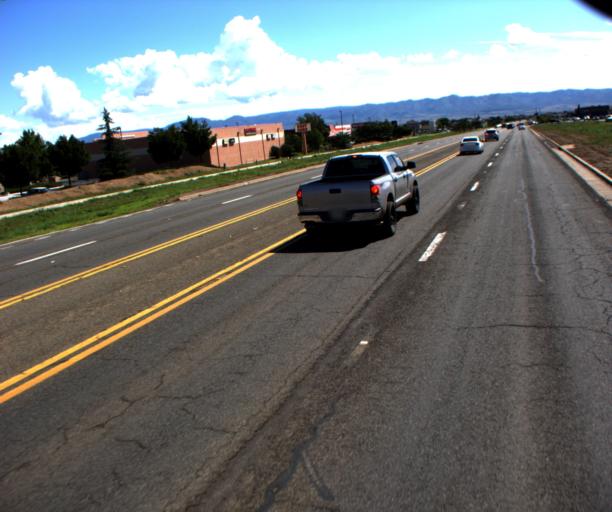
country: US
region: Arizona
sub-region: Yavapai County
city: Prescott Valley
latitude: 34.5839
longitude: -112.3381
